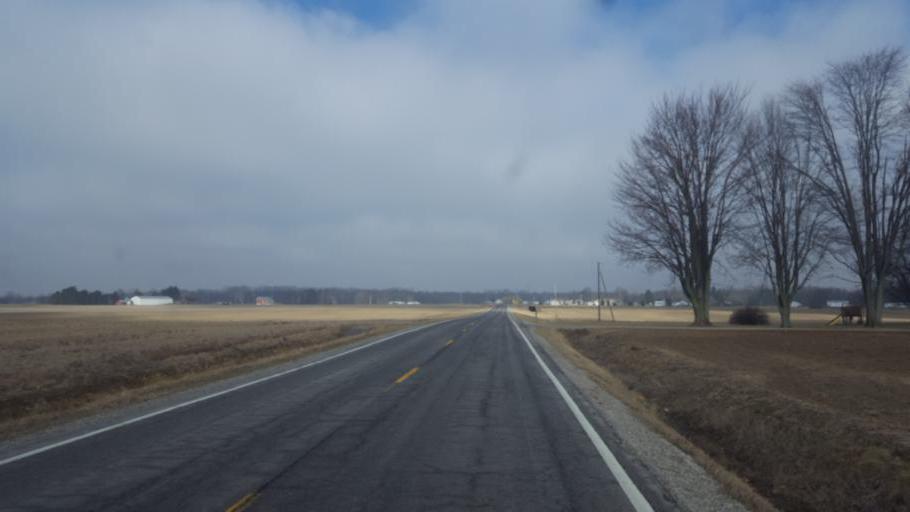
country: US
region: Ohio
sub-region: Crawford County
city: Bucyrus
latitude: 40.7362
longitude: -82.8979
